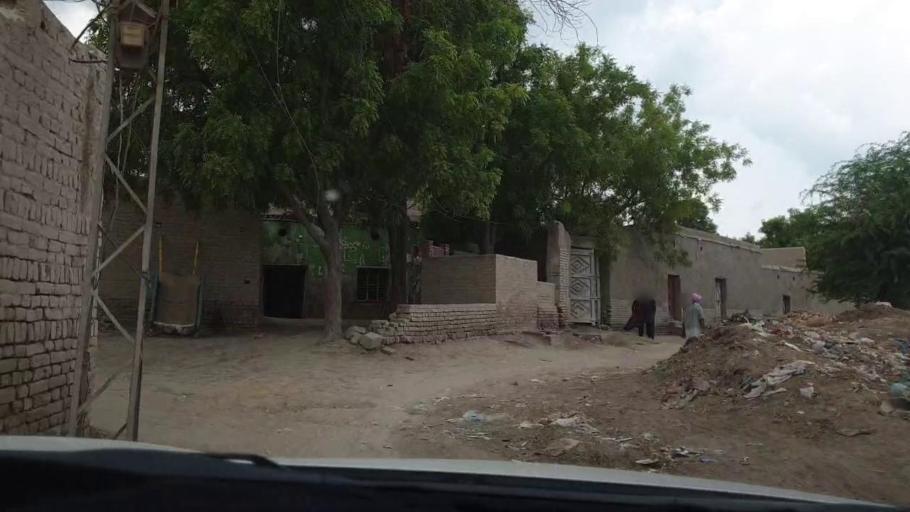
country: PK
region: Sindh
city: Dokri
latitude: 27.3254
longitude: 68.1037
